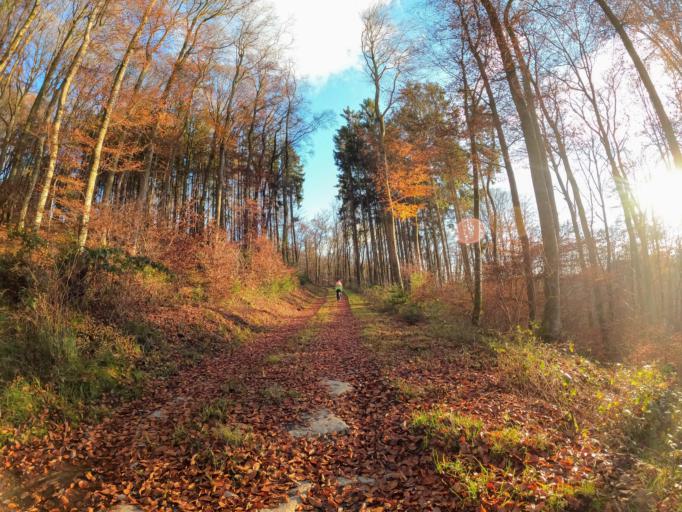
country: LU
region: Diekirch
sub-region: Canton de Wiltz
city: Bavigne
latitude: 49.9684
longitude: 5.8229
